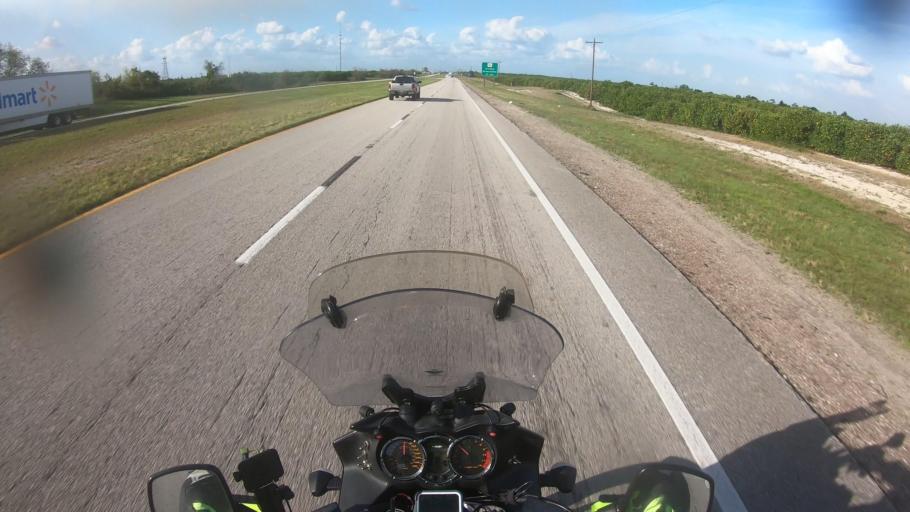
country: US
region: Florida
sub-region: Highlands County
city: Placid Lakes
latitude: 27.1998
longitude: -81.3291
